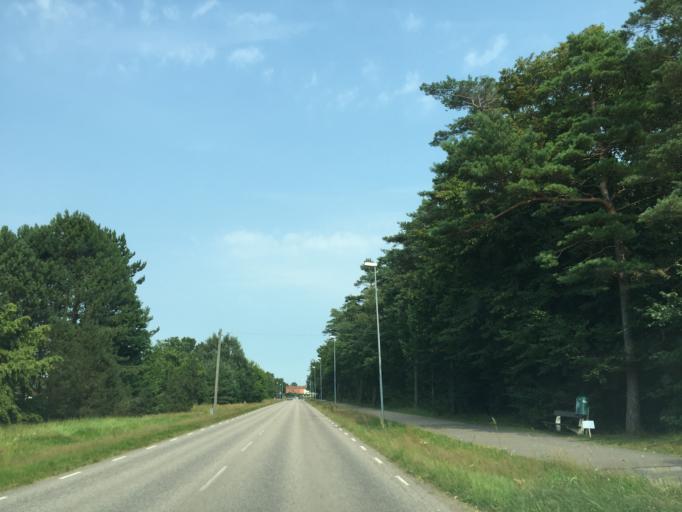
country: SE
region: Skane
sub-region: Angelholms Kommun
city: AEngelholm
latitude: 56.2307
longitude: 12.8453
